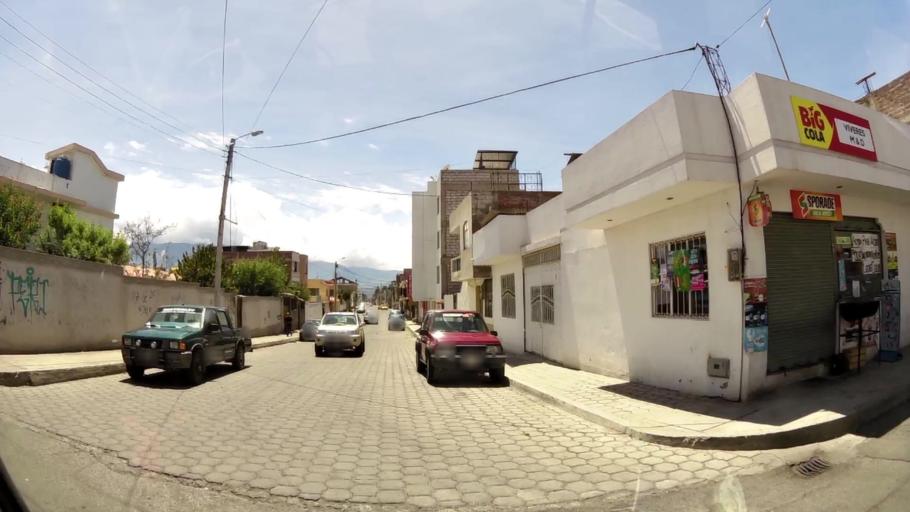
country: EC
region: Chimborazo
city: Riobamba
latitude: -1.6624
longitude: -78.6538
